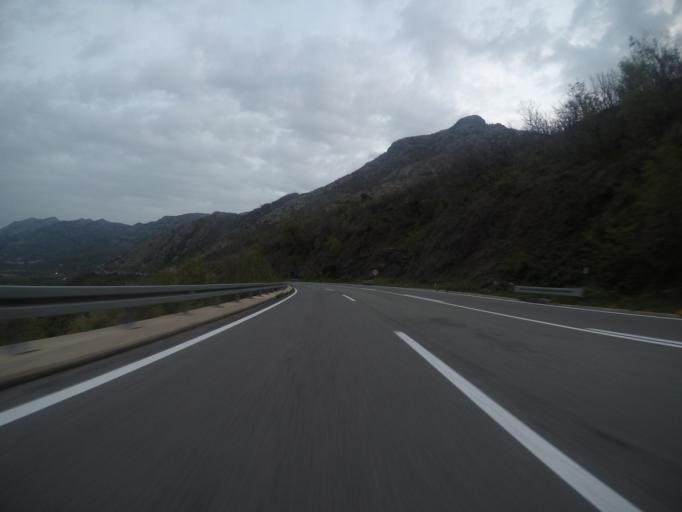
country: ME
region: Bar
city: Sutomore
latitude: 42.1765
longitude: 18.9973
